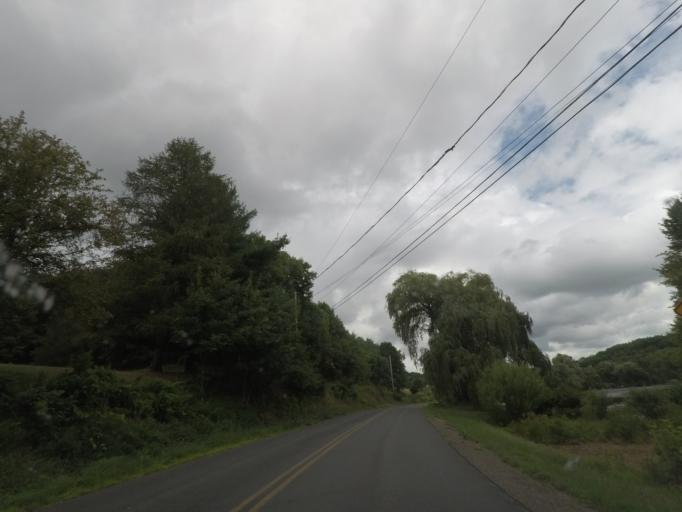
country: US
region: New York
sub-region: Rensselaer County
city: West Sand Lake
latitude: 42.6517
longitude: -73.6309
